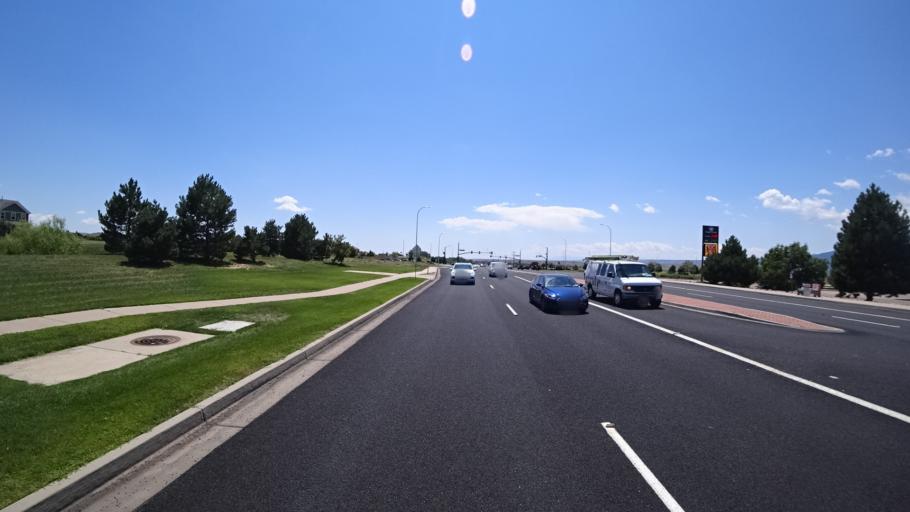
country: US
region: Colorado
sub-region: El Paso County
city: Stratmoor
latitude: 38.7822
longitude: -104.7388
